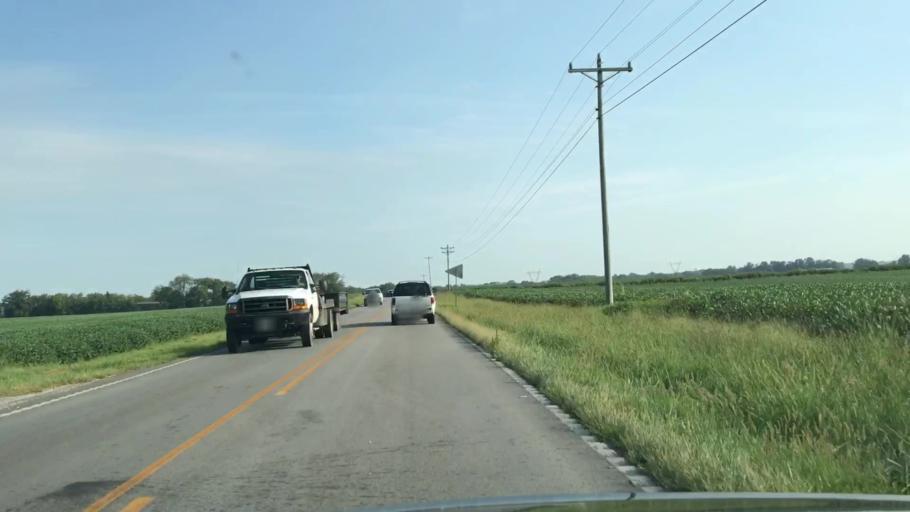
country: US
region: Kentucky
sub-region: Todd County
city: Guthrie
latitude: 36.6599
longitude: -87.1991
